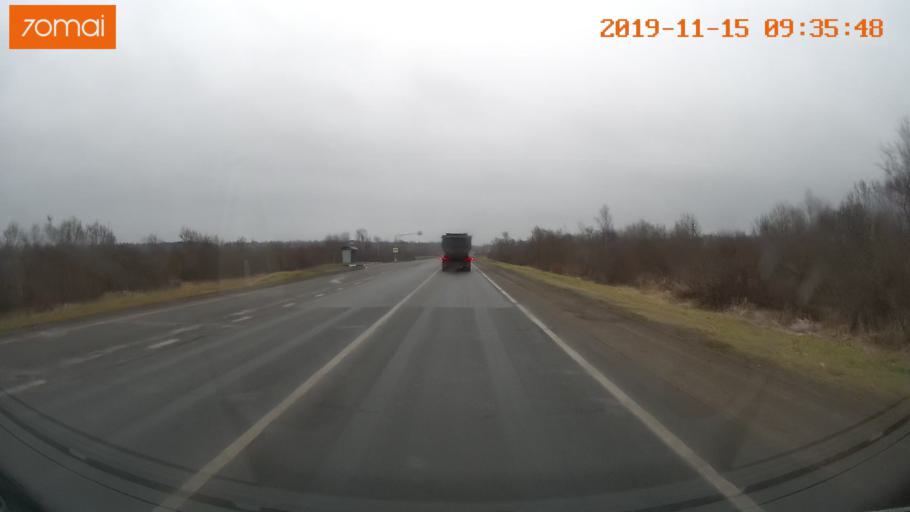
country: RU
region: Vologda
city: Sheksna
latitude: 59.2523
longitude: 38.4066
